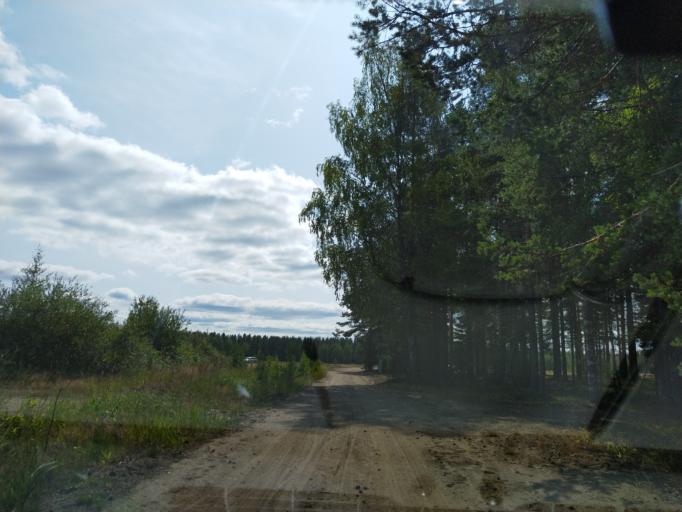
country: FI
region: Uusimaa
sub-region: Helsinki
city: Kaerkoelae
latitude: 60.7449
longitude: 24.1028
